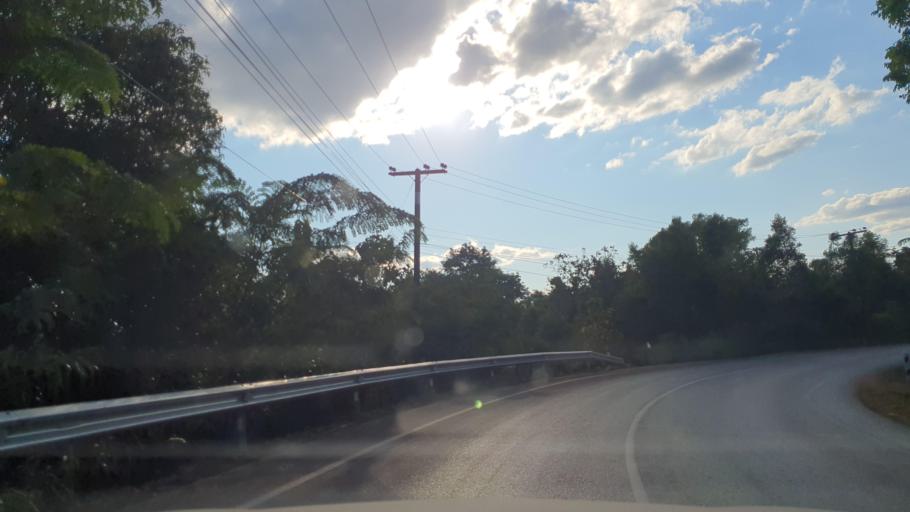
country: TH
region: Changwat Bueng Kan
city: Si Wilai
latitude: 18.1286
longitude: 103.8815
